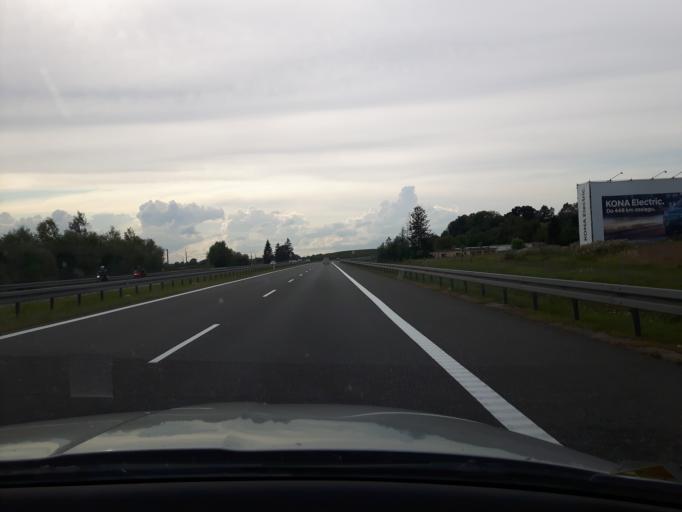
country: PL
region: Warmian-Masurian Voivodeship
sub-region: Powiat elblaski
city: Gronowo Gorne
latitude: 54.1088
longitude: 19.4933
